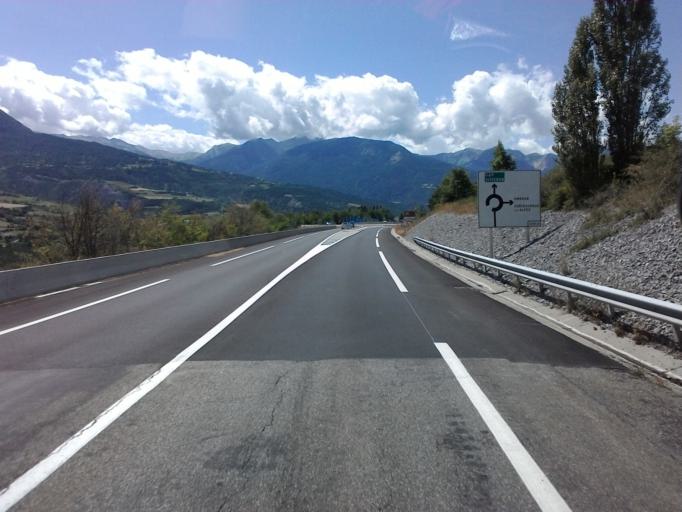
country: FR
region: Provence-Alpes-Cote d'Azur
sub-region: Departement des Hautes-Alpes
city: Embrun
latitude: 44.5885
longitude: 6.5138
